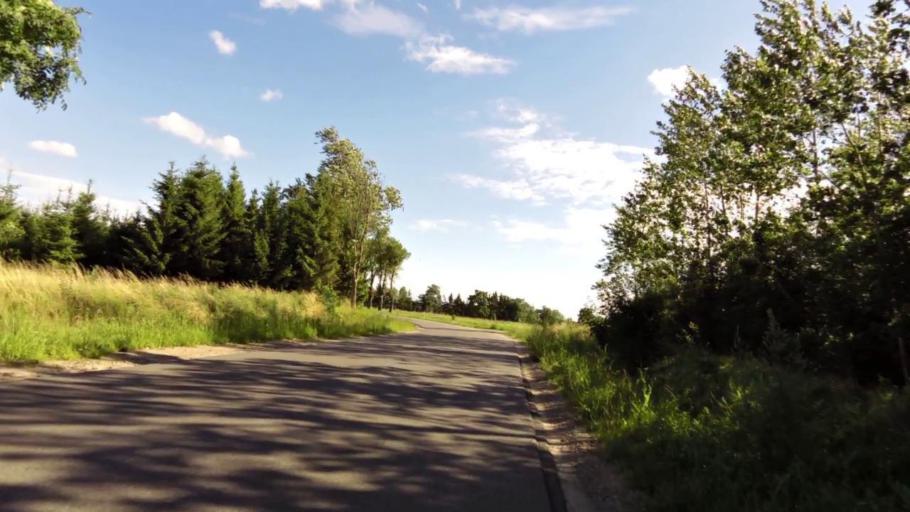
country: PL
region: West Pomeranian Voivodeship
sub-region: Powiat slawienski
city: Slawno
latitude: 54.4373
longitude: 16.7326
